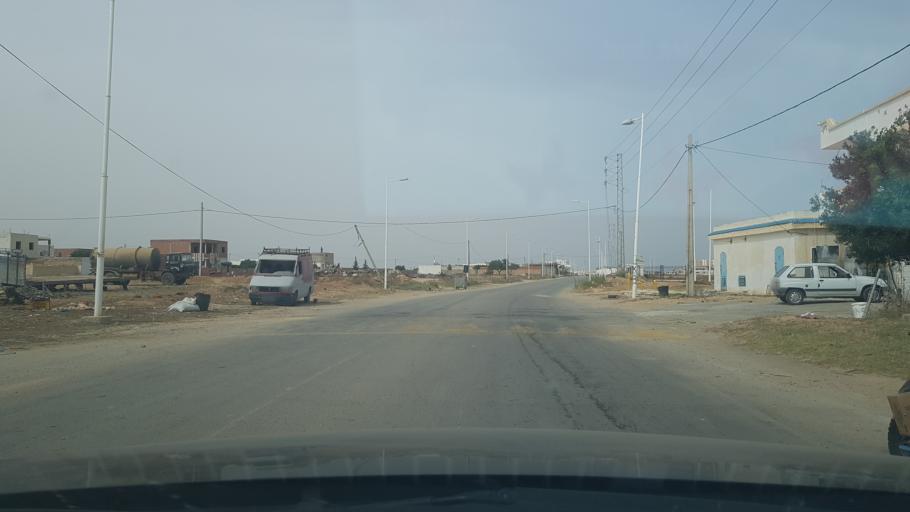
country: TN
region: Safaqis
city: Al Qarmadah
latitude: 34.8358
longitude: 10.7472
